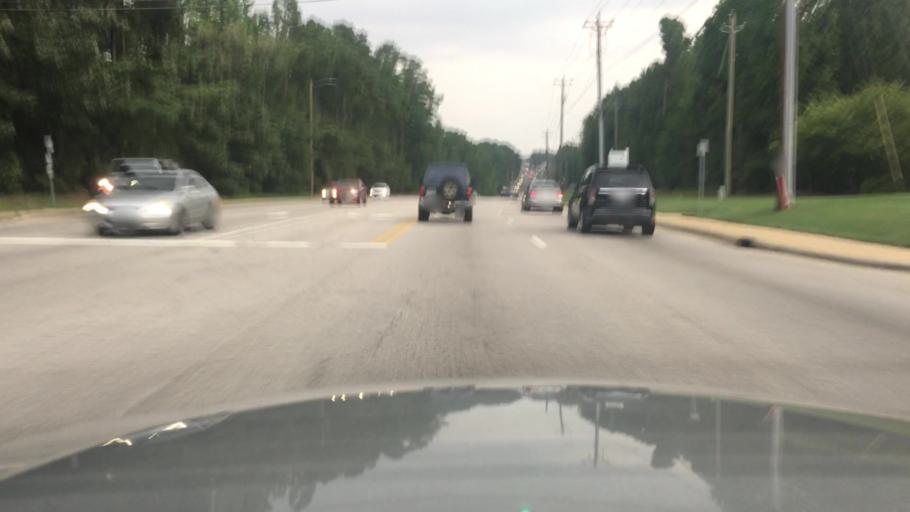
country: US
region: North Carolina
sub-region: Cumberland County
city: Fort Bragg
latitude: 35.0774
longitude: -79.0104
